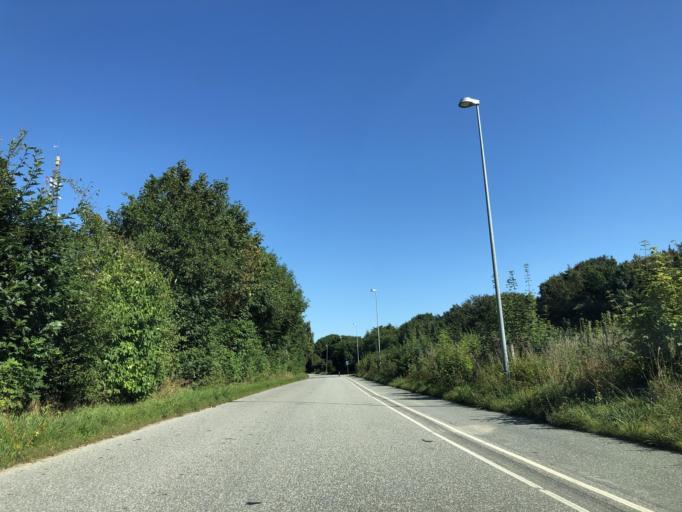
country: DK
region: North Denmark
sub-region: Mariagerfjord Kommune
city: Hobro
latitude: 56.6399
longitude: 9.7734
